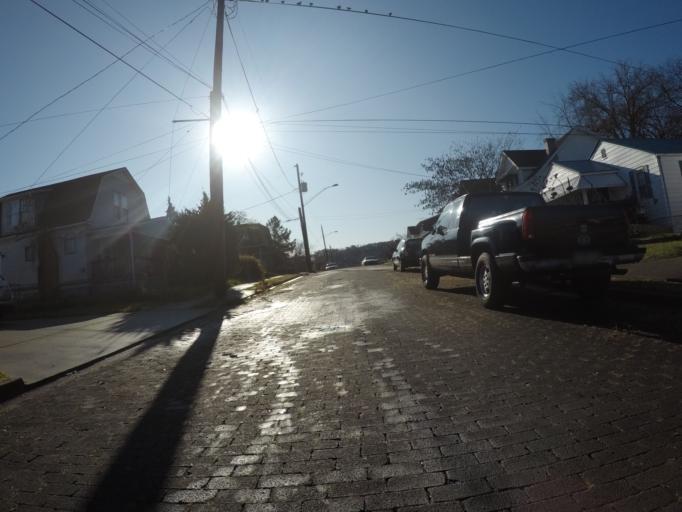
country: US
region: Ohio
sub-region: Lawrence County
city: Burlington
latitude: 38.4097
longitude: -82.4956
